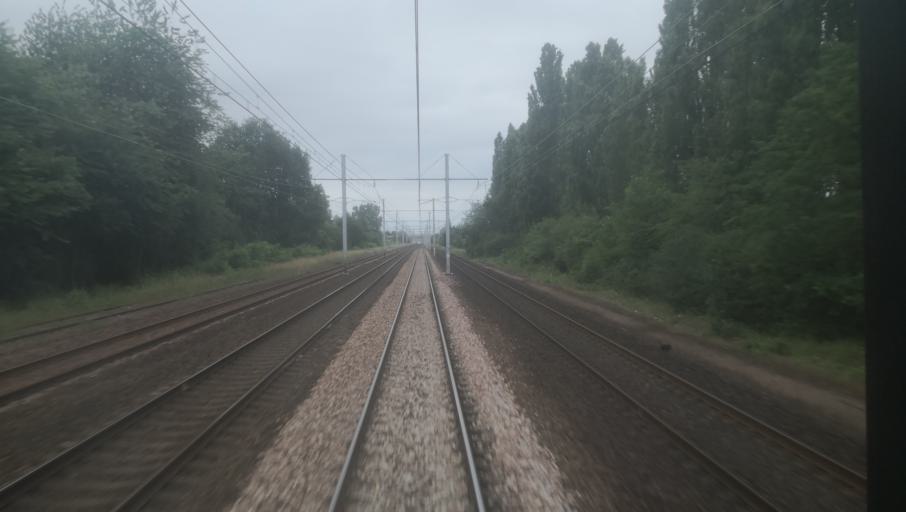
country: FR
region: Ile-de-France
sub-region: Departement de l'Essonne
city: Marolles-en-Hurepoix
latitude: 48.5691
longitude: 2.2906
